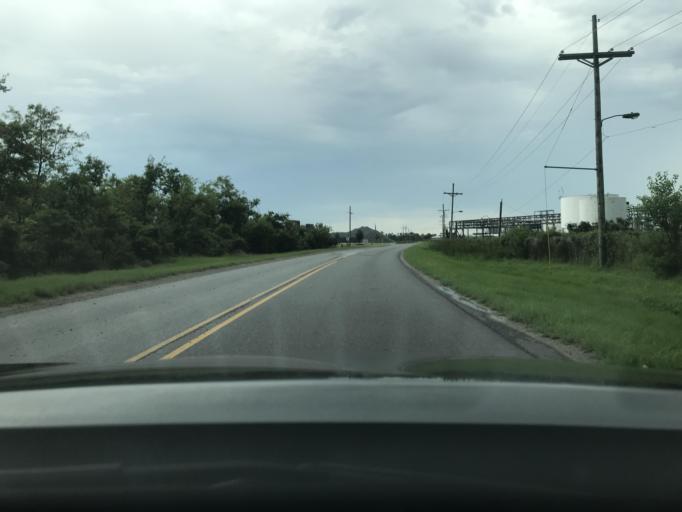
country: US
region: Louisiana
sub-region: Calcasieu Parish
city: Westlake
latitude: 30.2339
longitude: -93.2531
